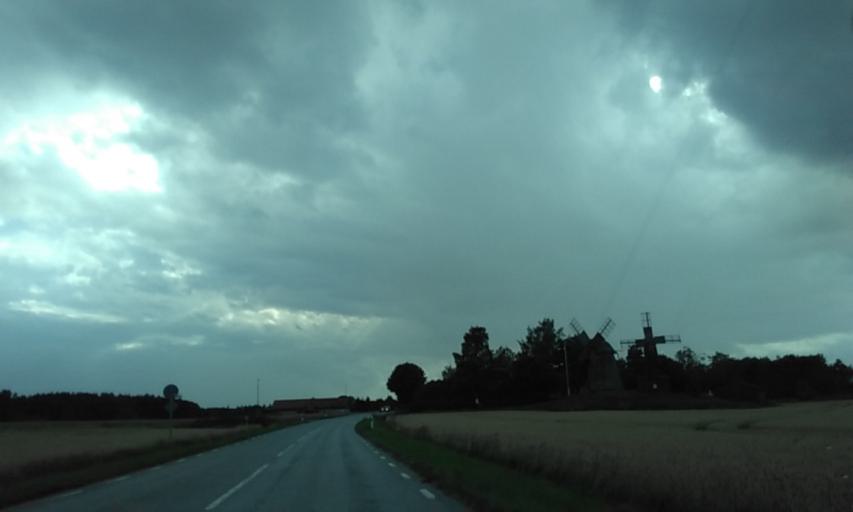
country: SE
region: Vaestra Goetaland
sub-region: Lidkopings Kommun
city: Lidkoping
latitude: 58.5066
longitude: 13.0011
